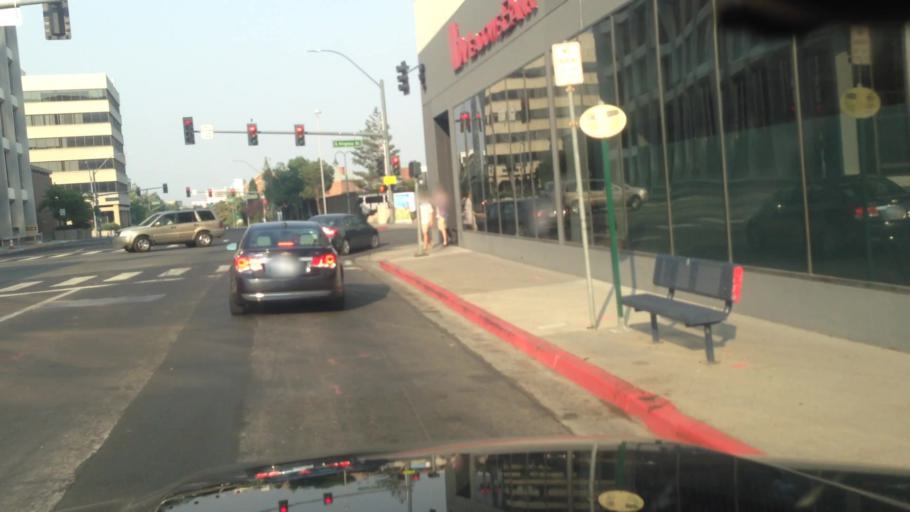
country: US
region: Nevada
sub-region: Washoe County
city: Reno
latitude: 39.5218
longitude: -119.8116
